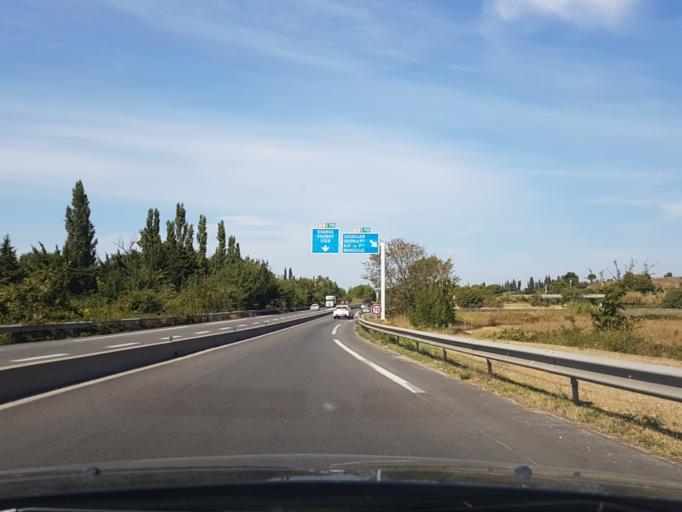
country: FR
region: Provence-Alpes-Cote d'Azur
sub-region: Departement des Bouches-du-Rhone
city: Noves
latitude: 43.8939
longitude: 4.9154
